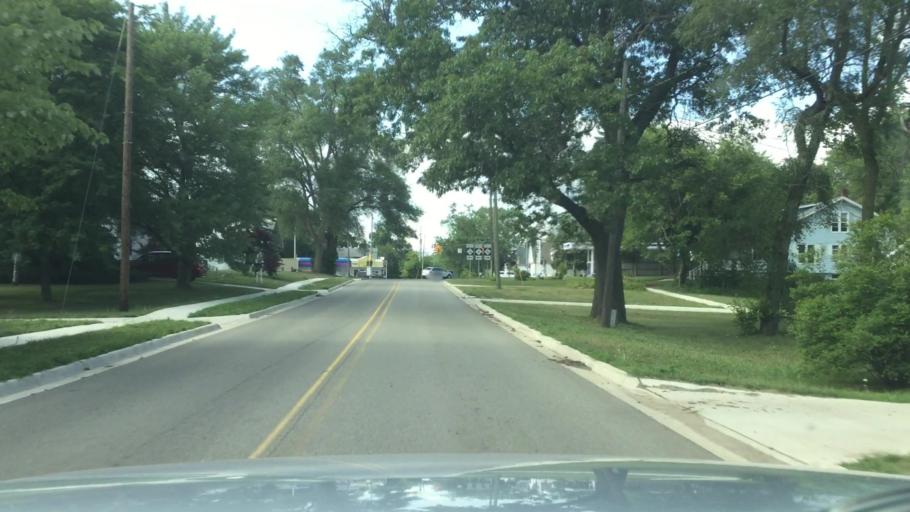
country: US
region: Michigan
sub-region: Ionia County
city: Belding
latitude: 43.0873
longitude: -85.2289
